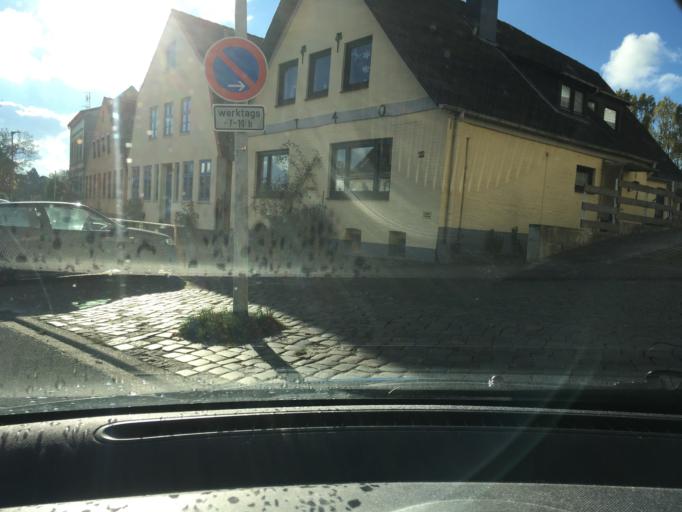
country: DE
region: Schleswig-Holstein
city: Busdorf
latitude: 54.4999
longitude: 9.5473
